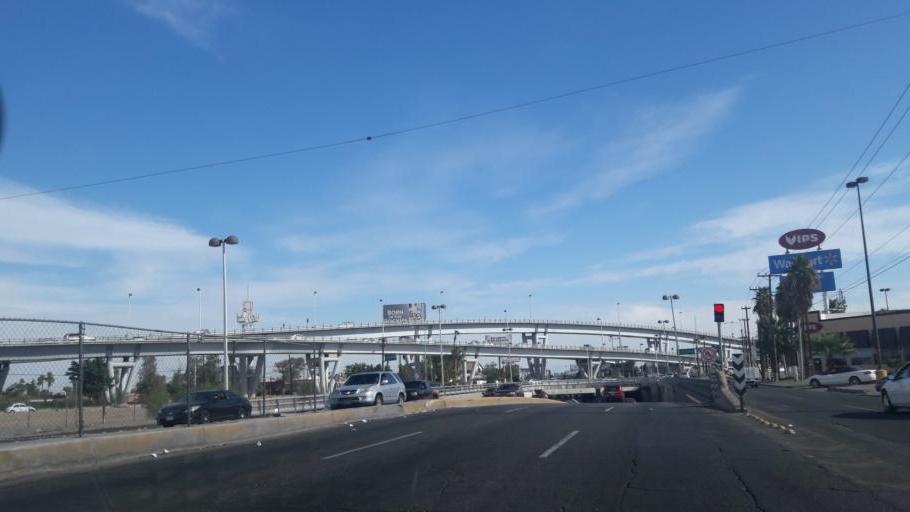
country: MX
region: Baja California
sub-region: Mexicali
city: Mexicali
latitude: 32.6247
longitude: -115.4551
